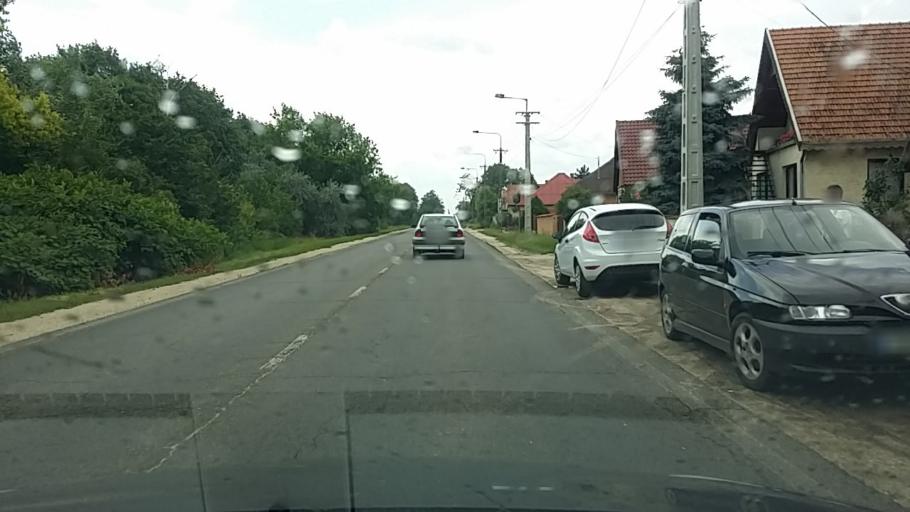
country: HU
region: Pest
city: Orkeny
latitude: 47.1324
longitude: 19.4177
